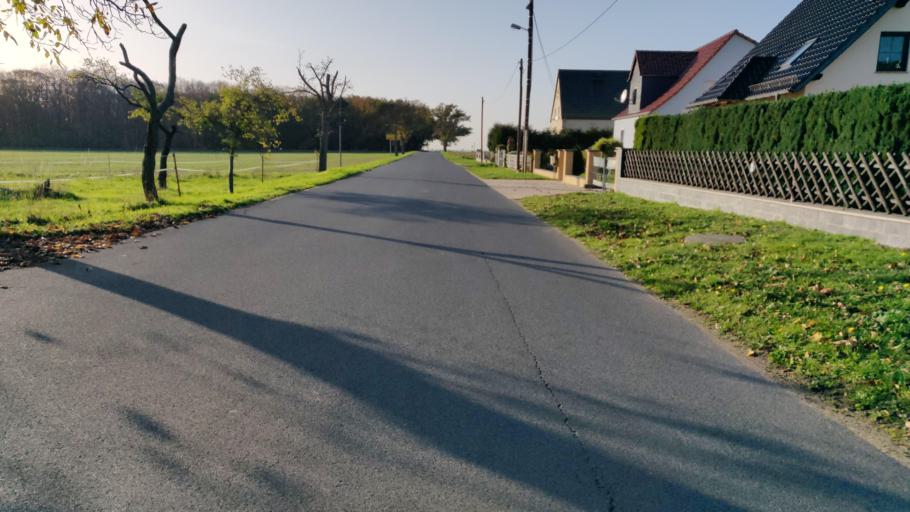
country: DE
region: Saxony
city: Lampertswalde
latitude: 51.3411
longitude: 13.6541
